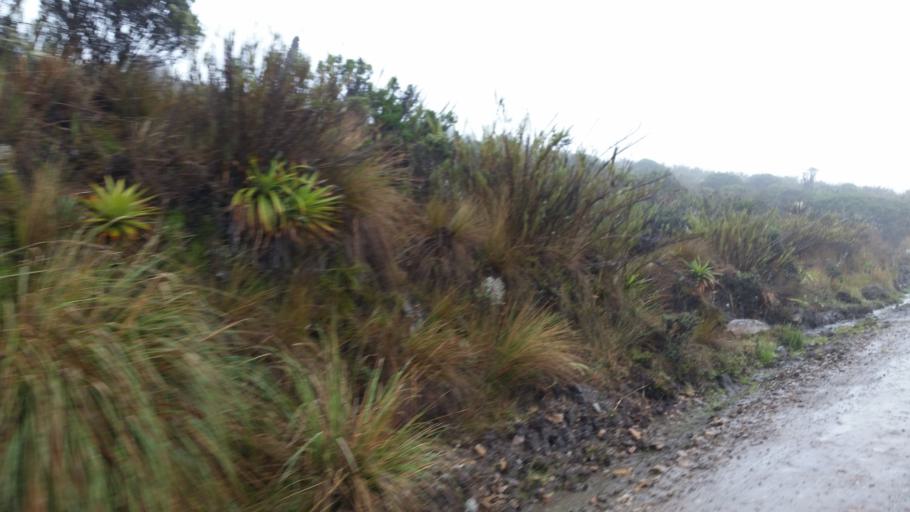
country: CO
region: Cundinamarca
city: La Calera
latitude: 4.6925
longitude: -73.8022
